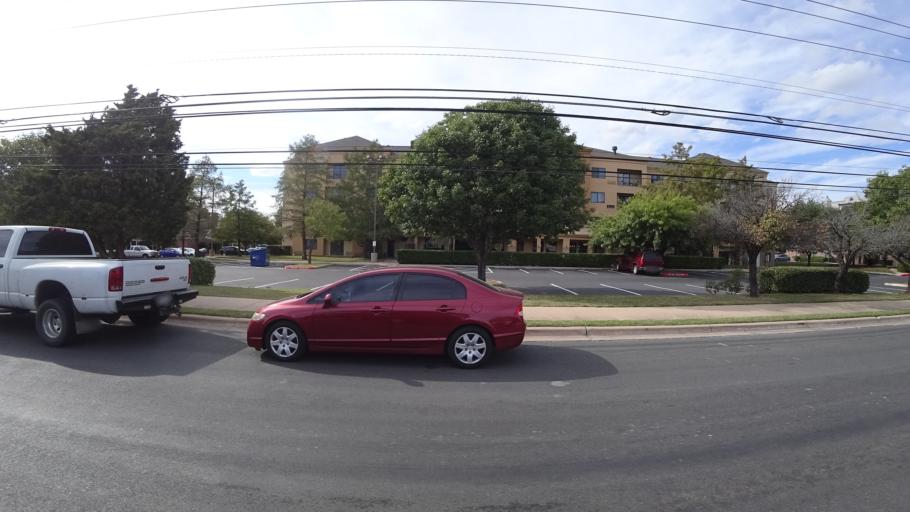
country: US
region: Texas
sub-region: Travis County
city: Austin
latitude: 30.2088
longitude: -97.7538
